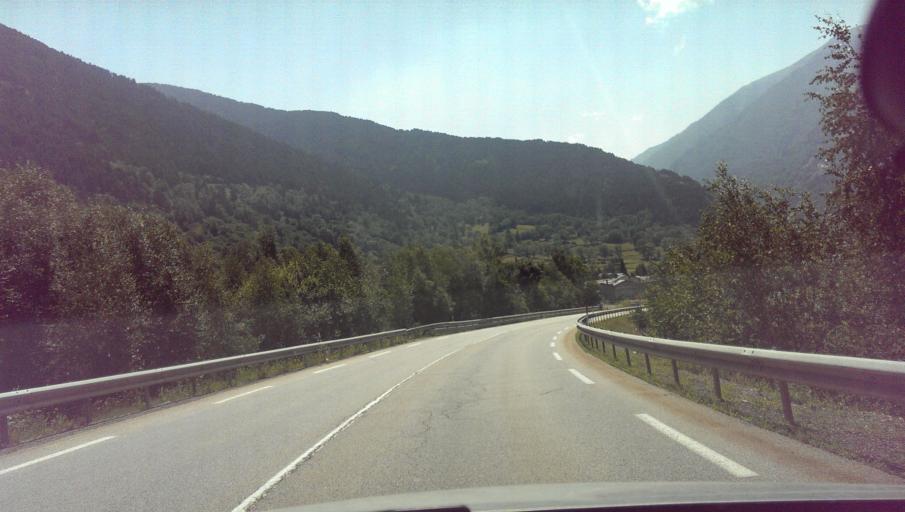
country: ES
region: Catalonia
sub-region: Provincia de Girona
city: Meranges
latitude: 42.5290
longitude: 1.8241
